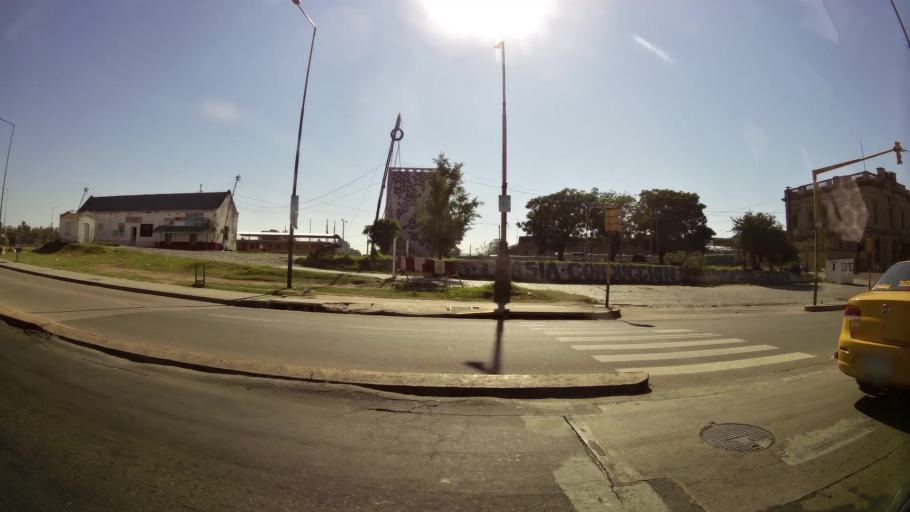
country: AR
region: Cordoba
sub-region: Departamento de Capital
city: Cordoba
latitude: -31.4195
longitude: -64.1758
